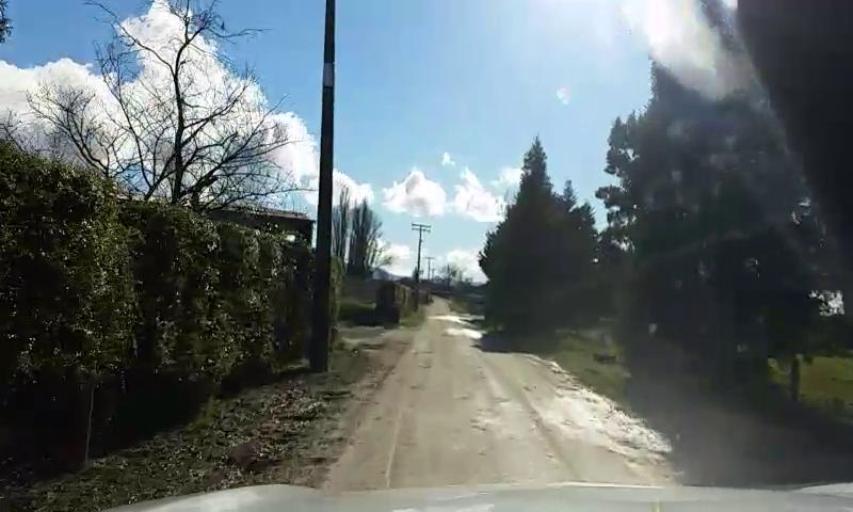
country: NZ
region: Tasman
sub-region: Tasman District
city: Richmond
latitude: -41.3010
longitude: 173.1424
